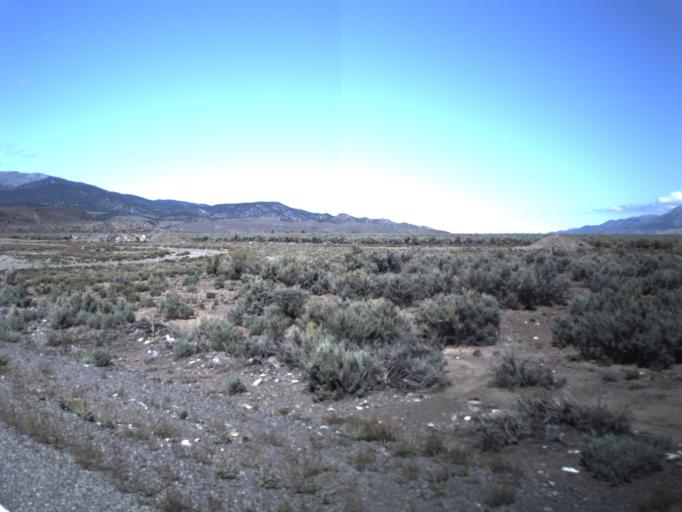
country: US
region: Utah
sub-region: Piute County
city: Junction
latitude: 38.2504
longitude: -112.2390
